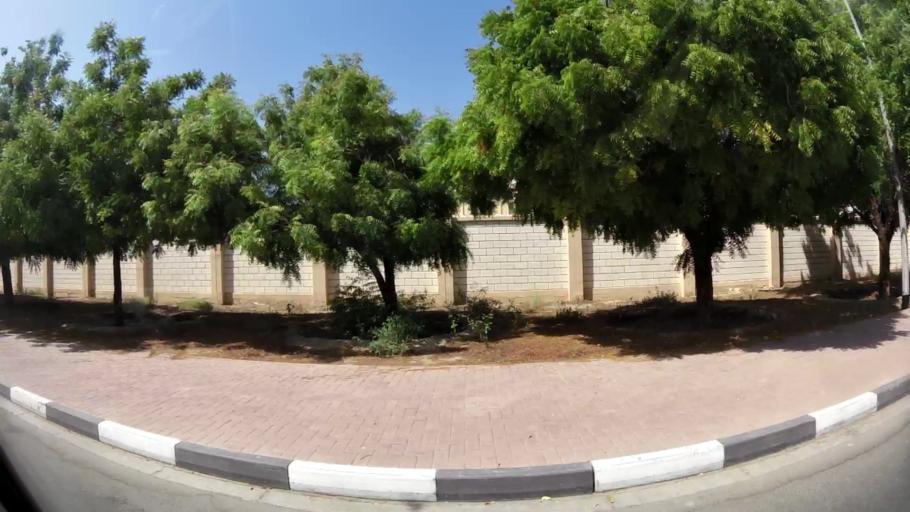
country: AE
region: Ash Shariqah
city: Sharjah
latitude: 25.2708
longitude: 55.3636
